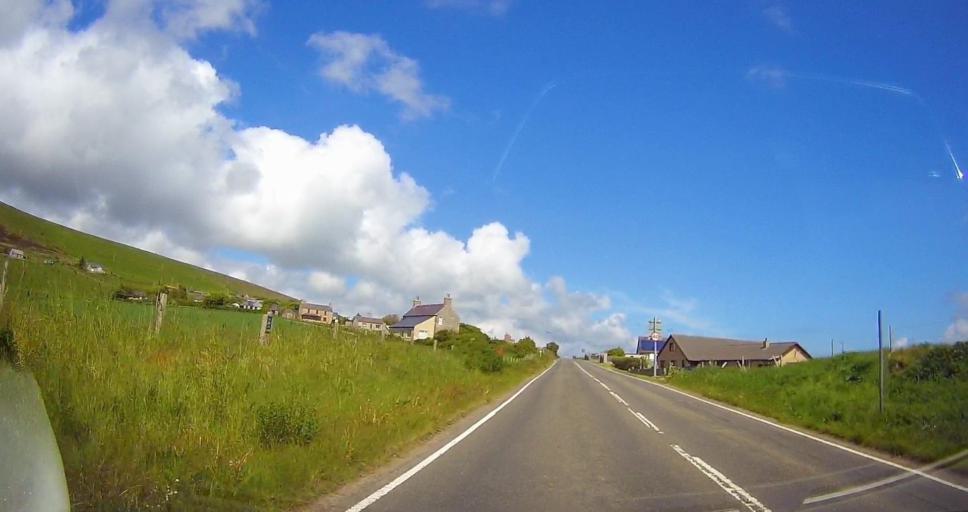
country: GB
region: Scotland
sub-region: Orkney Islands
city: Orkney
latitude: 59.0114
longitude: -3.1122
